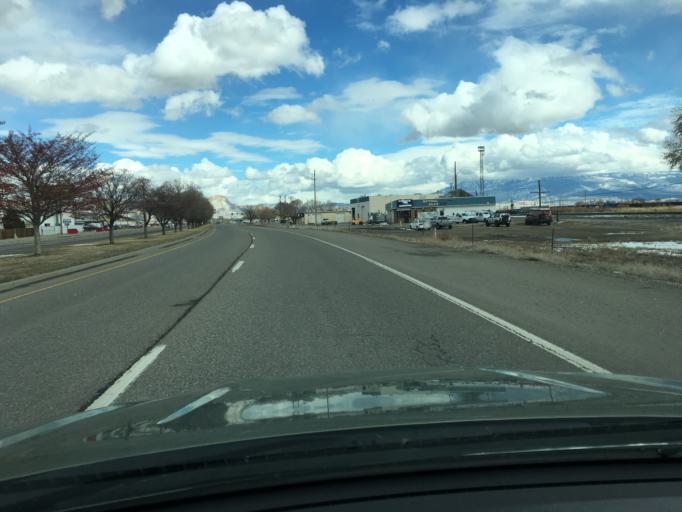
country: US
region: Colorado
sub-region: Mesa County
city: Grand Junction
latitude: 39.0653
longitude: -108.5463
